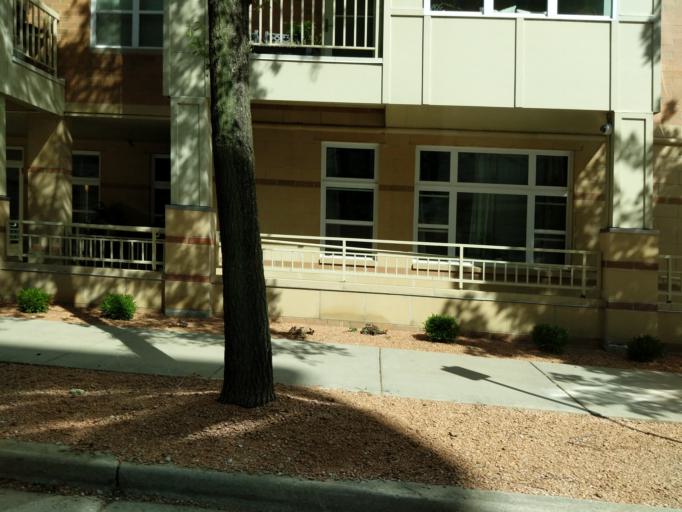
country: US
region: Wisconsin
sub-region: Milwaukee County
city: Milwaukee
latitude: 43.0562
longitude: -87.8991
